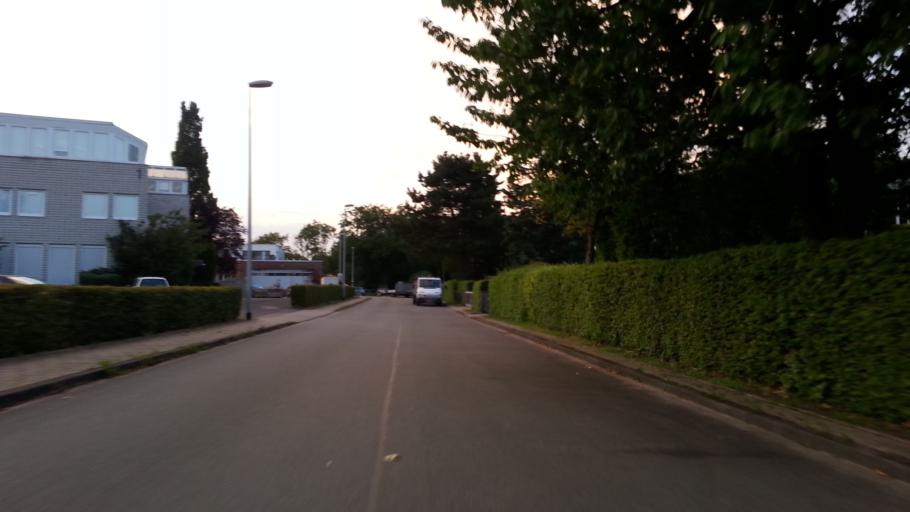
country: DE
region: North Rhine-Westphalia
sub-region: Regierungsbezirk Munster
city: Muenster
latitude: 51.9458
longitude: 7.5315
